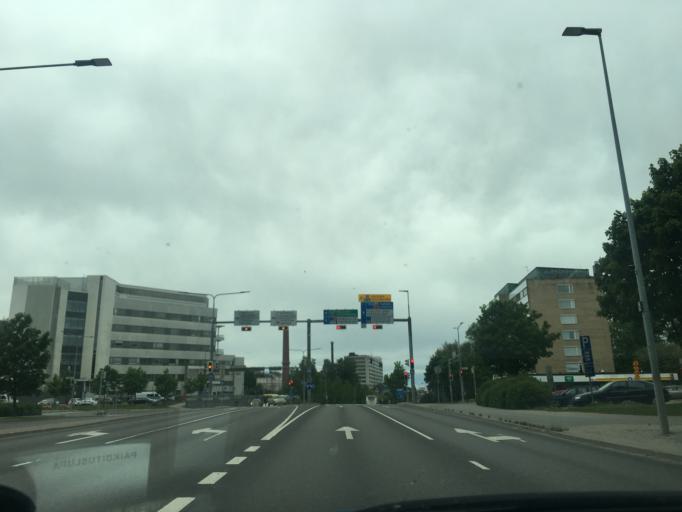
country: FI
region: Varsinais-Suomi
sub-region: Turku
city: Turku
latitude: 60.4558
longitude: 22.2987
